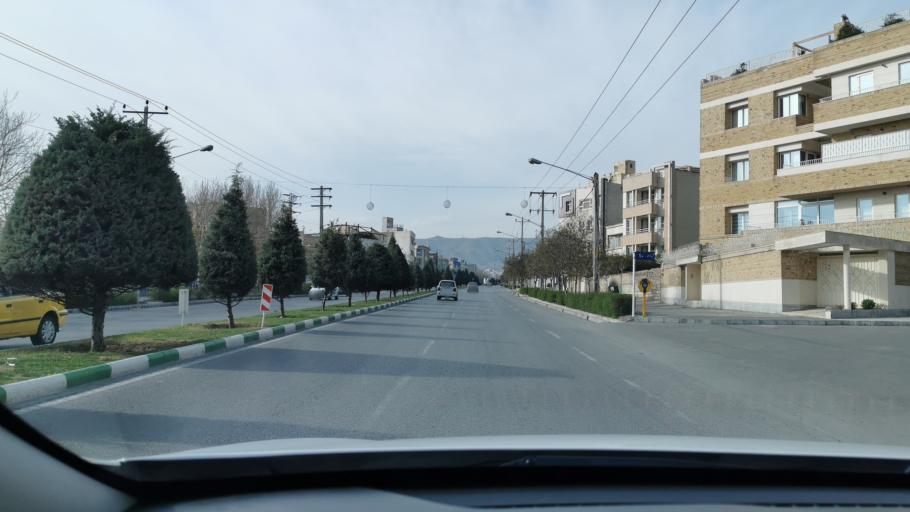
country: IR
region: Razavi Khorasan
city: Mashhad
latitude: 36.3081
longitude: 59.5145
